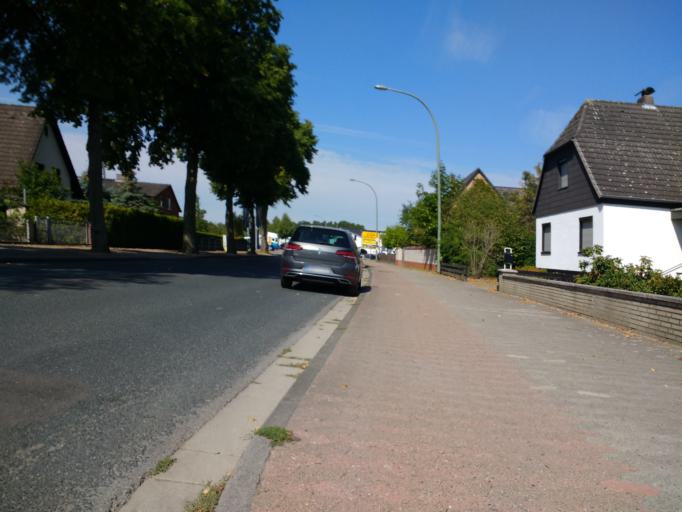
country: DE
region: Lower Saxony
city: Gifhorn
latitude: 52.4861
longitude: 10.5214
